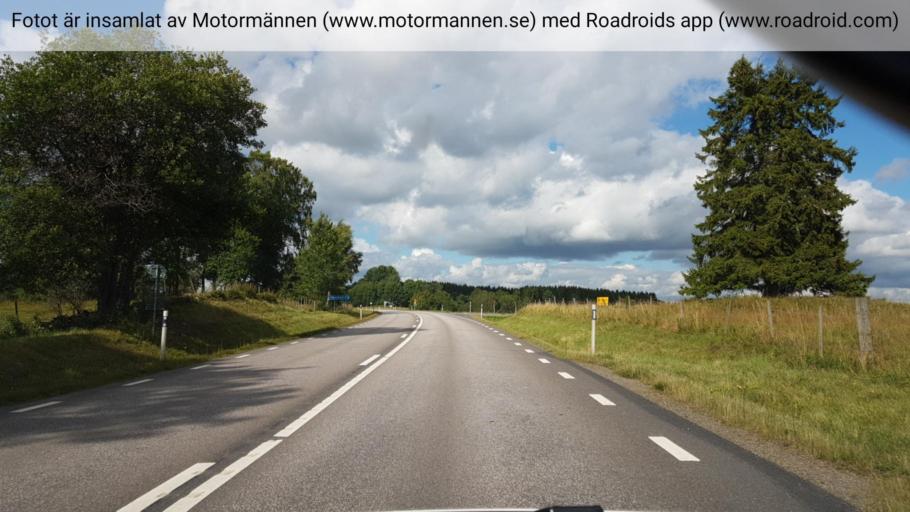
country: SE
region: Vaestra Goetaland
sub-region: Falkopings Kommun
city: Falkoeping
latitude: 58.0129
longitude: 13.5718
